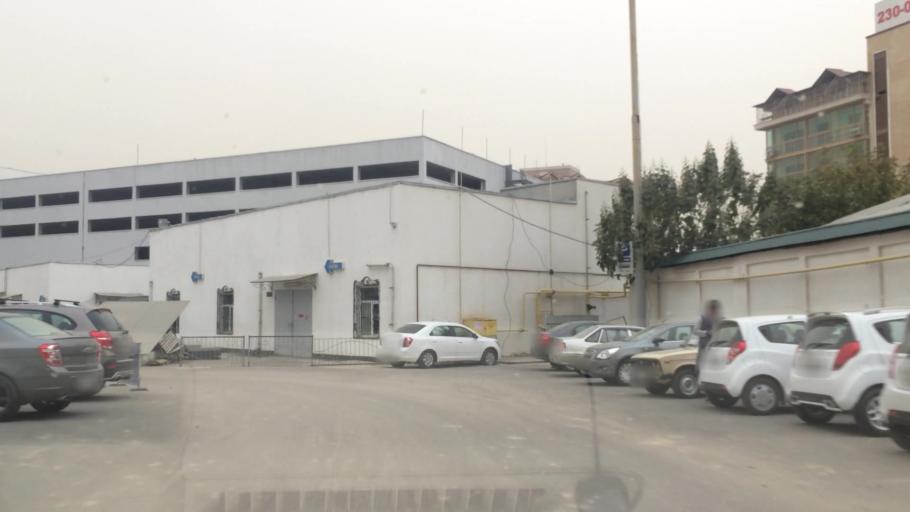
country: UZ
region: Toshkent Shahri
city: Tashkent
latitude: 41.2986
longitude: 69.2487
